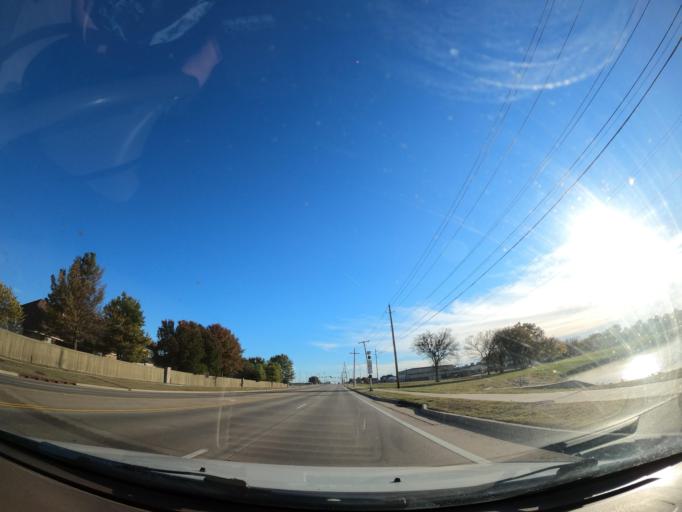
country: US
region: Oklahoma
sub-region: Tulsa County
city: Owasso
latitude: 36.2834
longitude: -95.8303
